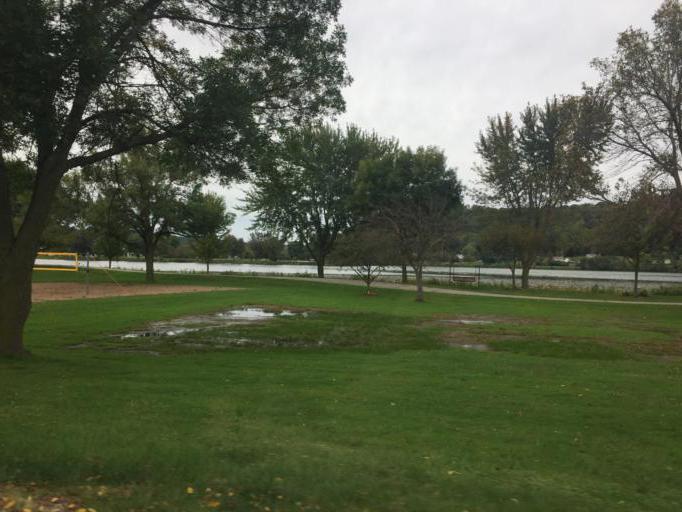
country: US
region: Minnesota
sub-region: Winona County
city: Winona
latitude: 44.0381
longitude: -91.6305
